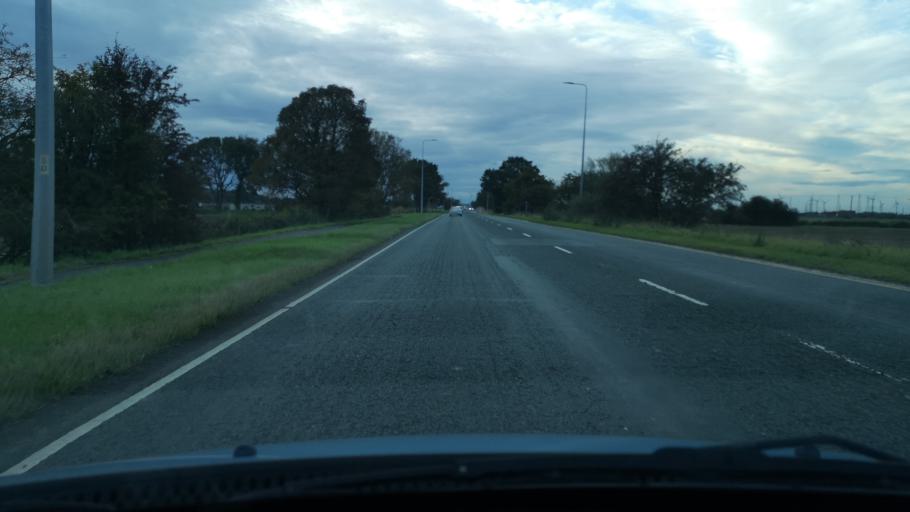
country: GB
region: England
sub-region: North Lincolnshire
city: Gunness
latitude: 53.5897
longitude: -0.7060
